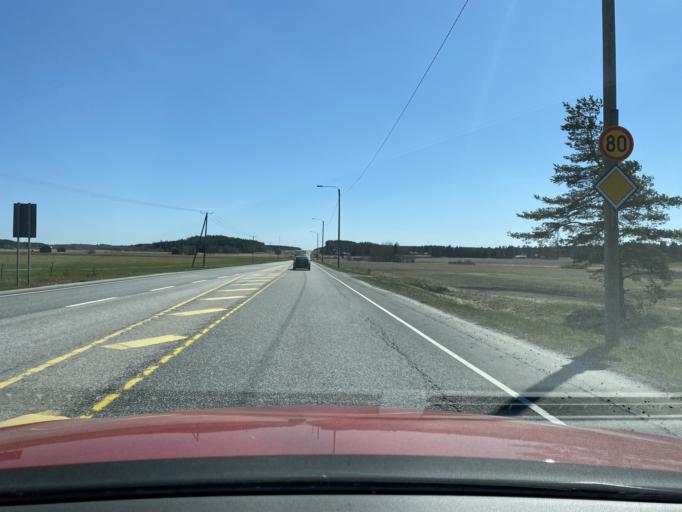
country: FI
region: Haeme
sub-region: Forssa
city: Jokioinen
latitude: 60.8715
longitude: 23.4940
